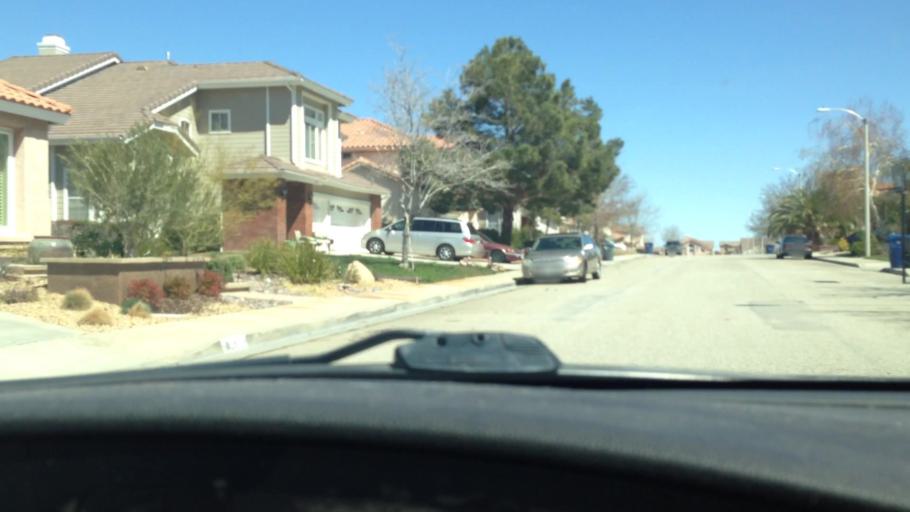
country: US
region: California
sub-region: Los Angeles County
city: Desert View Highlands
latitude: 34.5850
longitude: -118.1640
